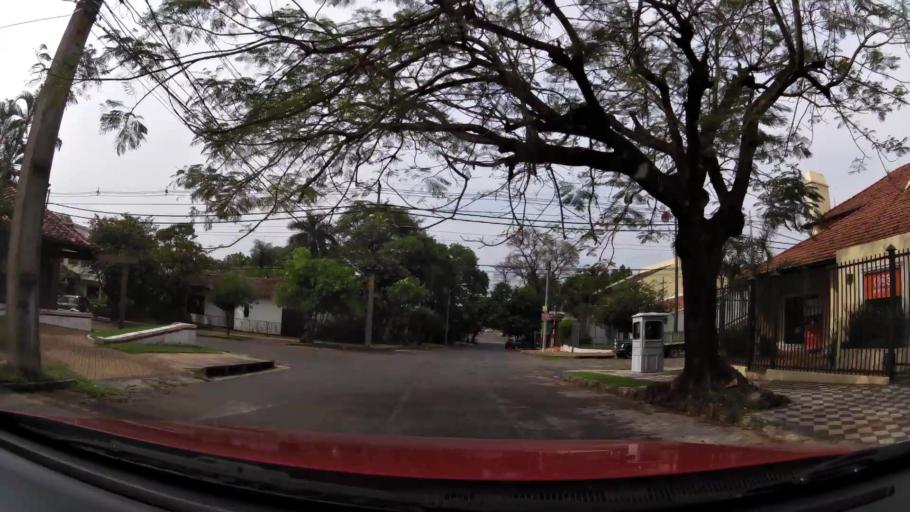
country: PY
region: Central
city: Lambare
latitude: -25.2939
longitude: -57.5737
